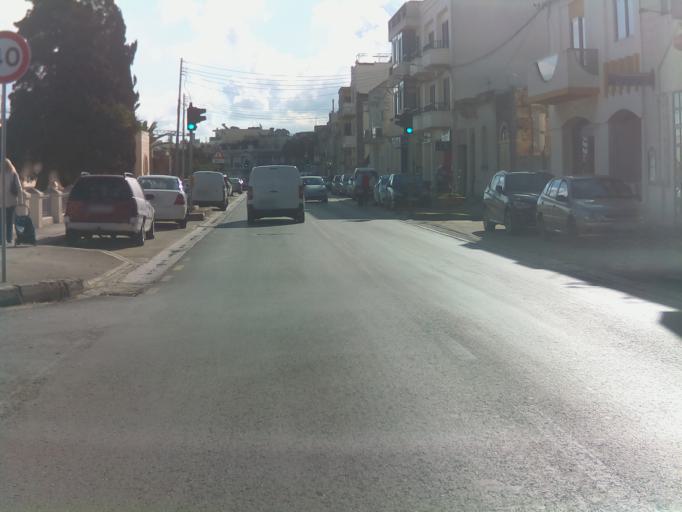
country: MT
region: Il-Mellieha
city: Mellieha
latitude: 35.9564
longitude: 14.3657
